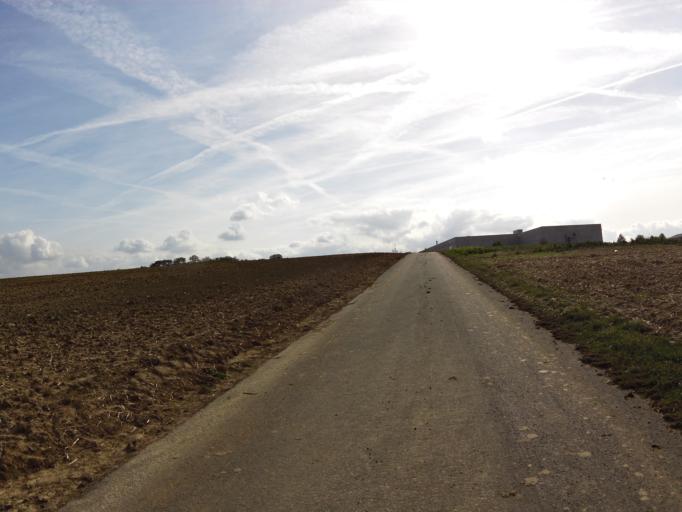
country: DE
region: Bavaria
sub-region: Regierungsbezirk Unterfranken
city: Giebelstadt
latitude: 49.6968
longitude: 9.9457
